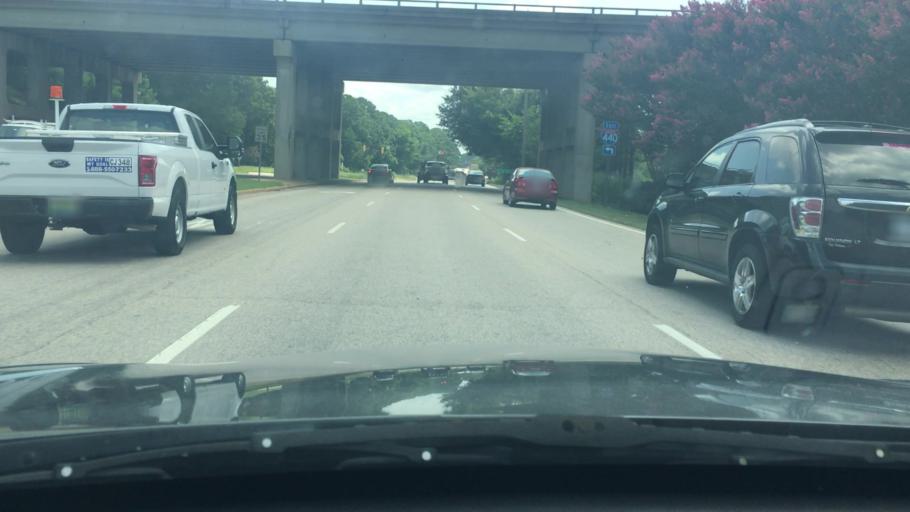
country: US
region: North Carolina
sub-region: Wake County
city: West Raleigh
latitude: 35.7956
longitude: -78.6955
